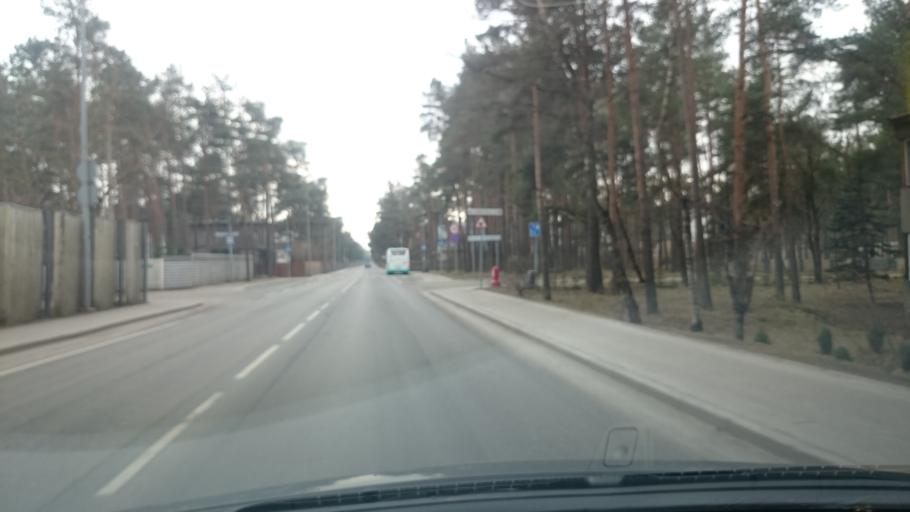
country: EE
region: Harju
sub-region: Saue vald
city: Laagri
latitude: 59.3831
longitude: 24.6385
